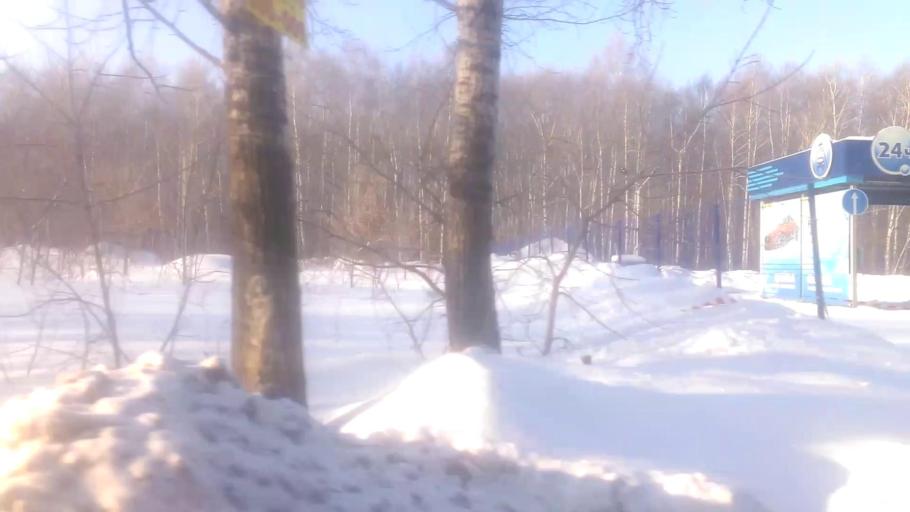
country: RU
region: Altai Krai
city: Novosilikatnyy
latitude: 53.3711
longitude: 83.6621
